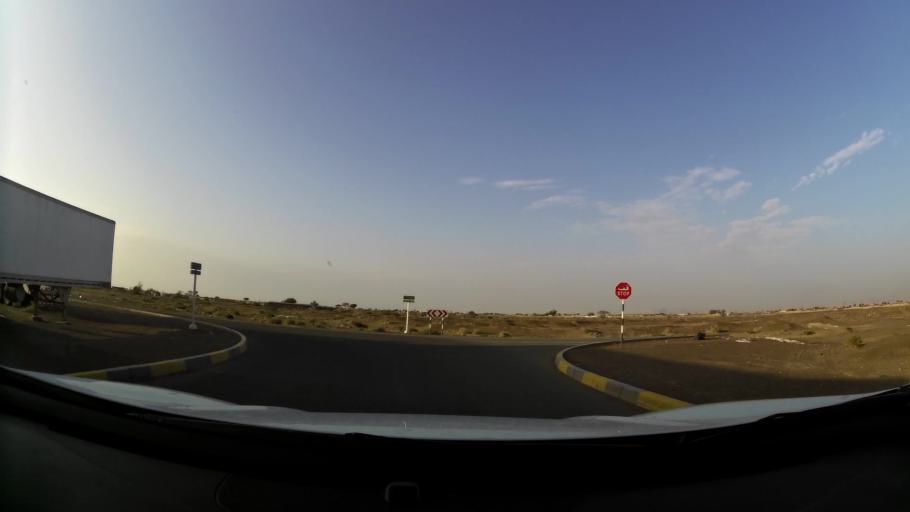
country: AE
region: Abu Dhabi
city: Al Ain
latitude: 24.1549
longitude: 55.8362
